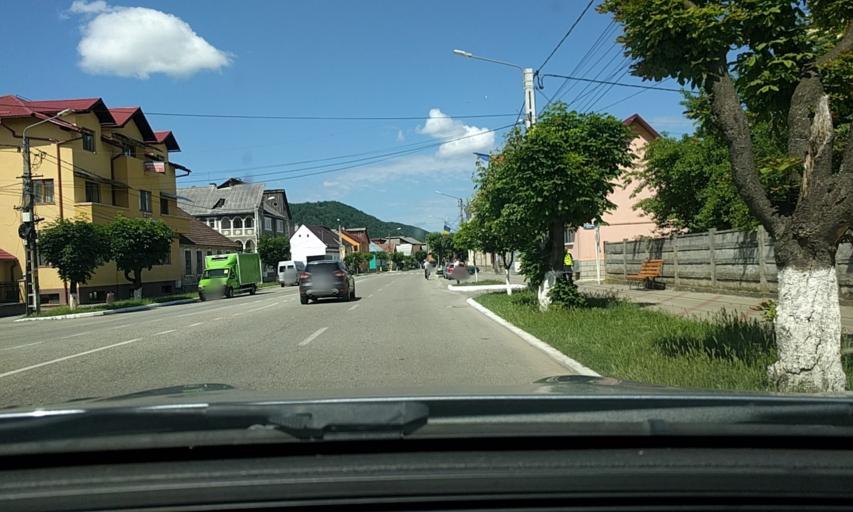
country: RO
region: Bistrita-Nasaud
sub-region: Oras Nasaud
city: Nasaud
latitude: 47.2868
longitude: 24.3981
